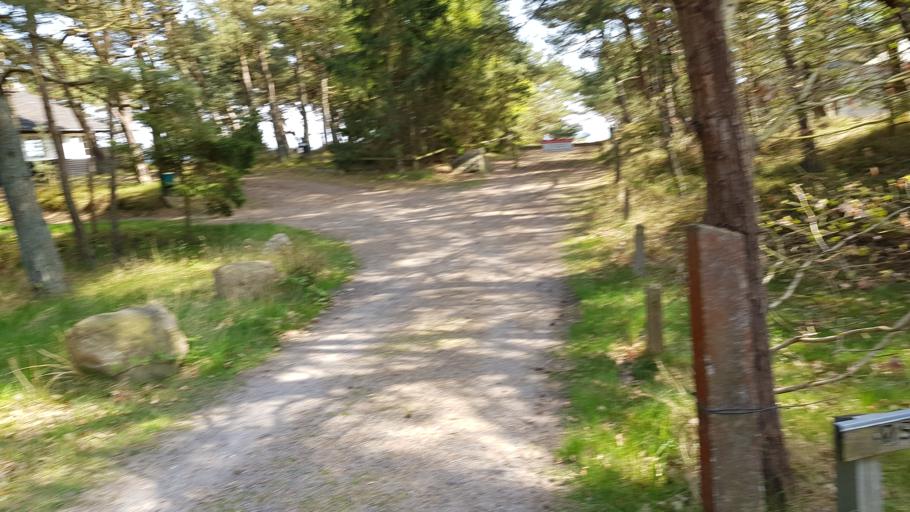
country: DK
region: Capital Region
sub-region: Bornholm Kommune
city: Nexo
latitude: 54.9997
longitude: 15.0919
